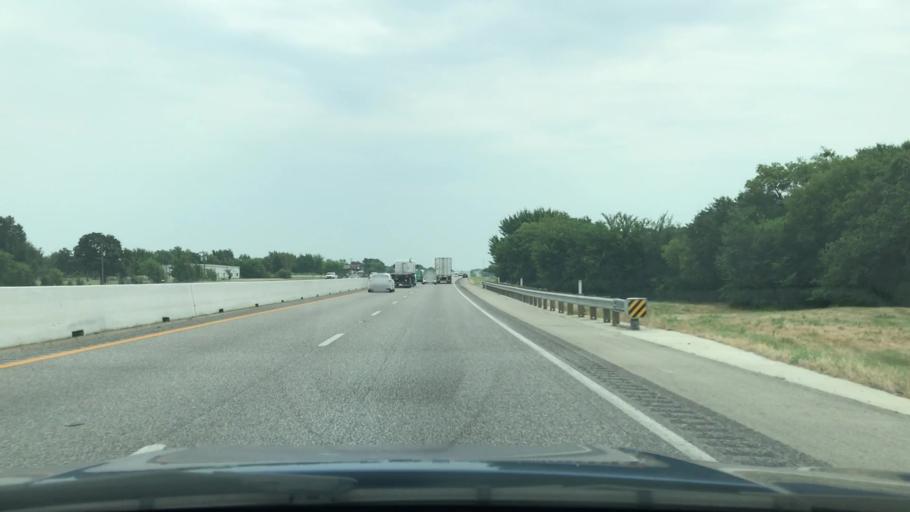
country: US
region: Texas
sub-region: Van Zandt County
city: Wills Point
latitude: 32.6447
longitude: -96.0535
